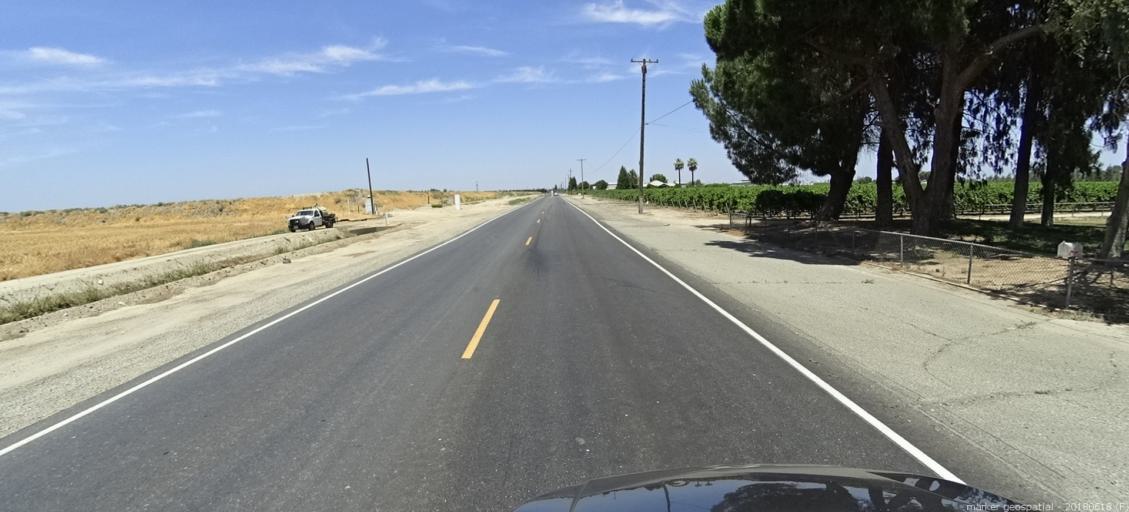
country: US
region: California
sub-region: Madera County
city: Madera
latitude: 36.9288
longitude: -120.0923
